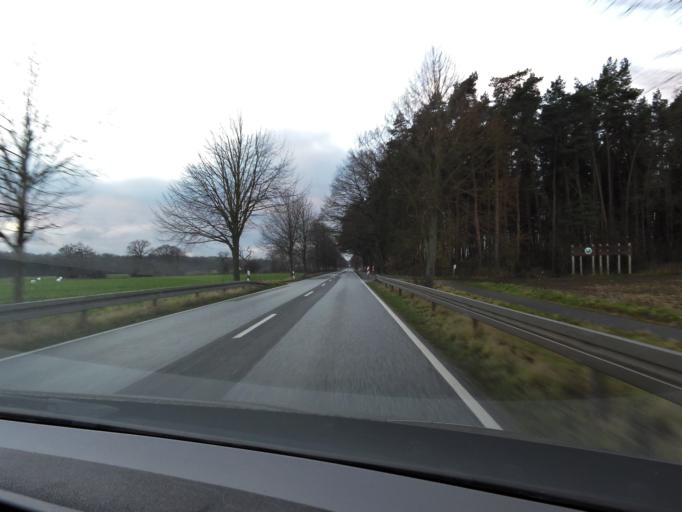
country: DE
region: Mecklenburg-Vorpommern
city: Roggendorf
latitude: 53.6948
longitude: 11.0357
